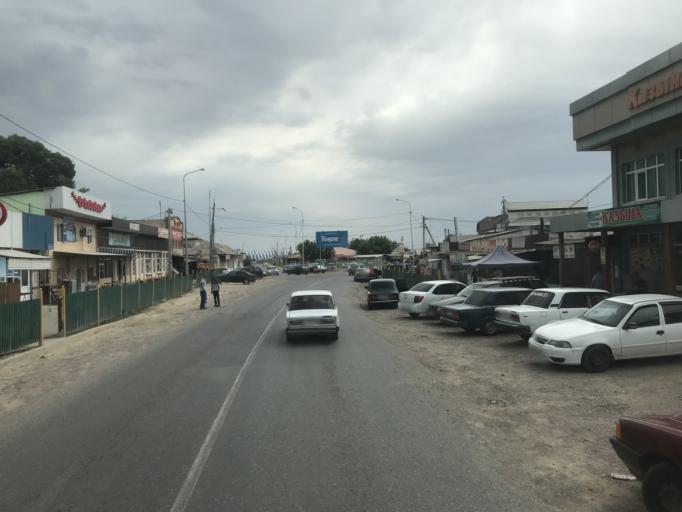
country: KZ
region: Ongtustik Qazaqstan
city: Saryaghash
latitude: 41.3391
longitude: 68.9515
